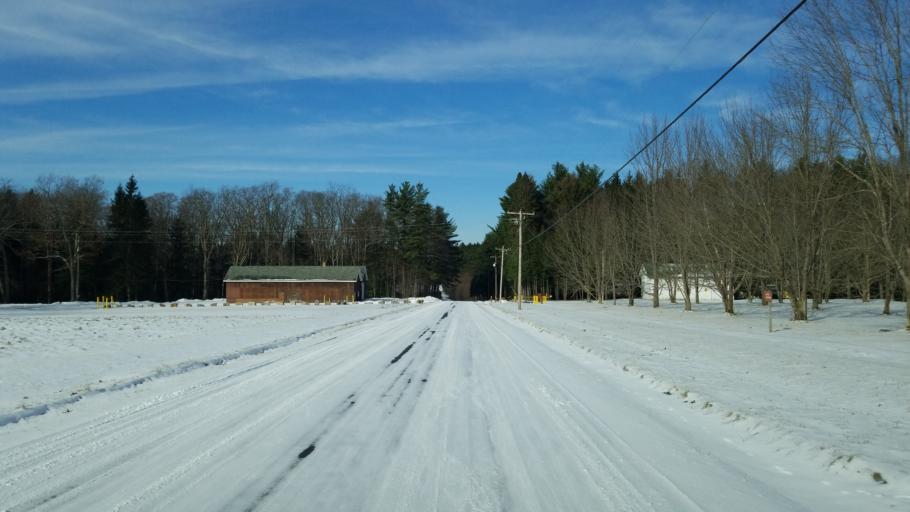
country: US
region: Pennsylvania
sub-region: Clearfield County
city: Clearfield
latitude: 41.1164
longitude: -78.5284
